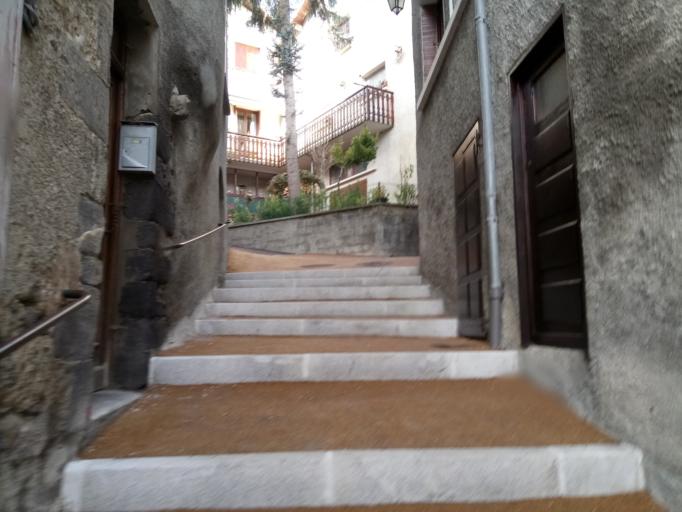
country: FR
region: Provence-Alpes-Cote d'Azur
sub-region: Departement des Alpes-de-Haute-Provence
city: Seyne-les-Alpes
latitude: 44.3508
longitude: 6.3559
